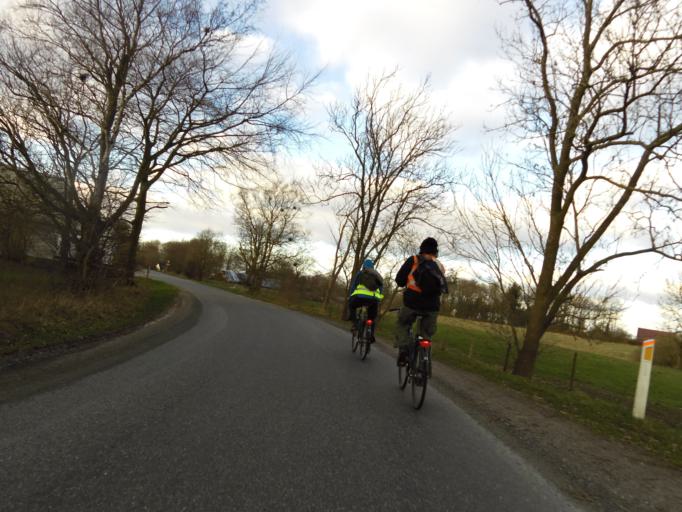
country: DK
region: South Denmark
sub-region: Esbjerg Kommune
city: Ribe
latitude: 55.3052
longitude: 8.8487
